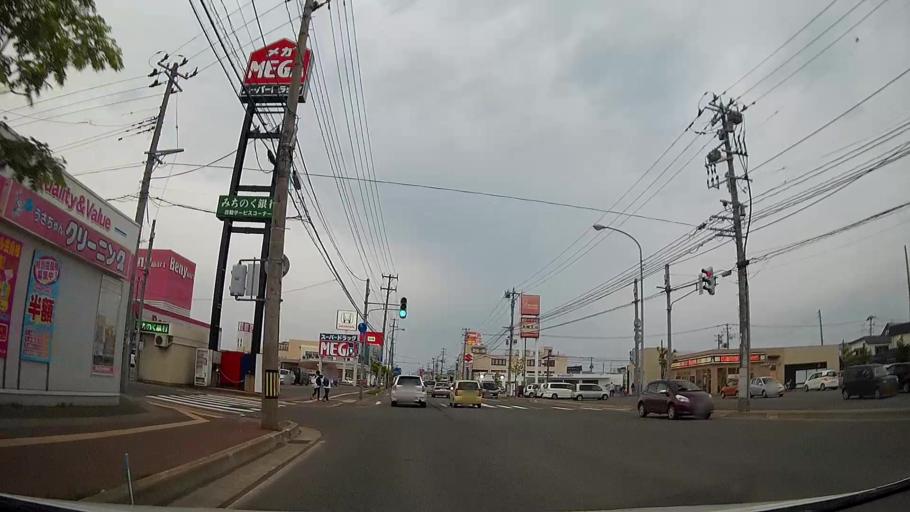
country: JP
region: Aomori
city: Aomori Shi
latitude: 40.8027
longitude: 140.7563
